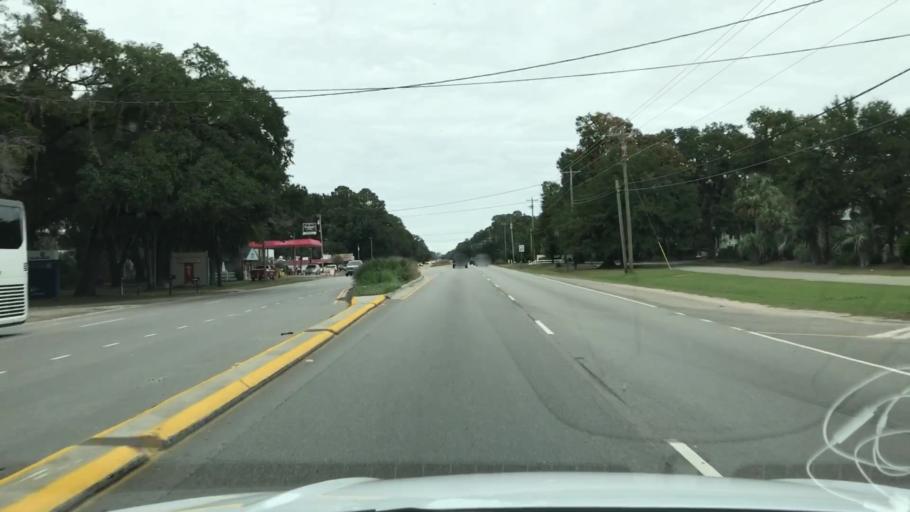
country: US
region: South Carolina
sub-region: Georgetown County
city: Murrells Inlet
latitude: 33.4588
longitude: -79.1133
